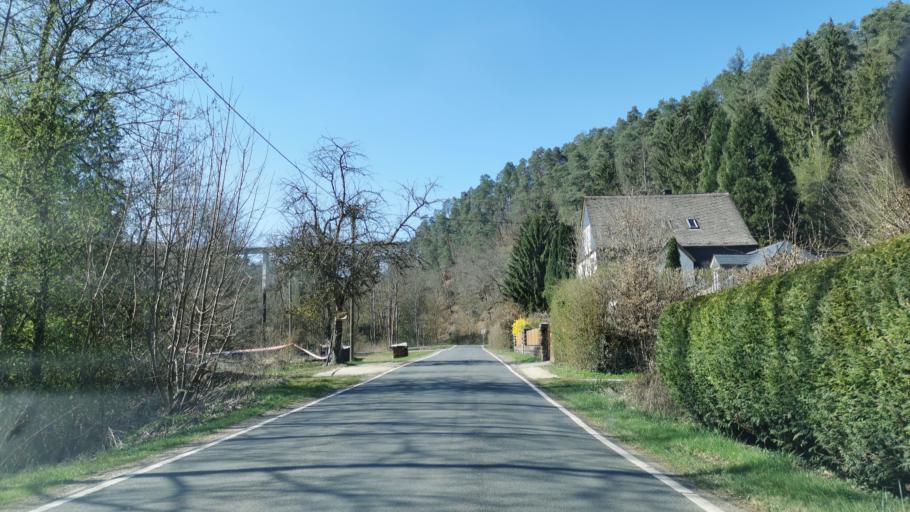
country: DE
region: Rheinland-Pfalz
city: Trier
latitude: 49.7836
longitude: 6.6498
